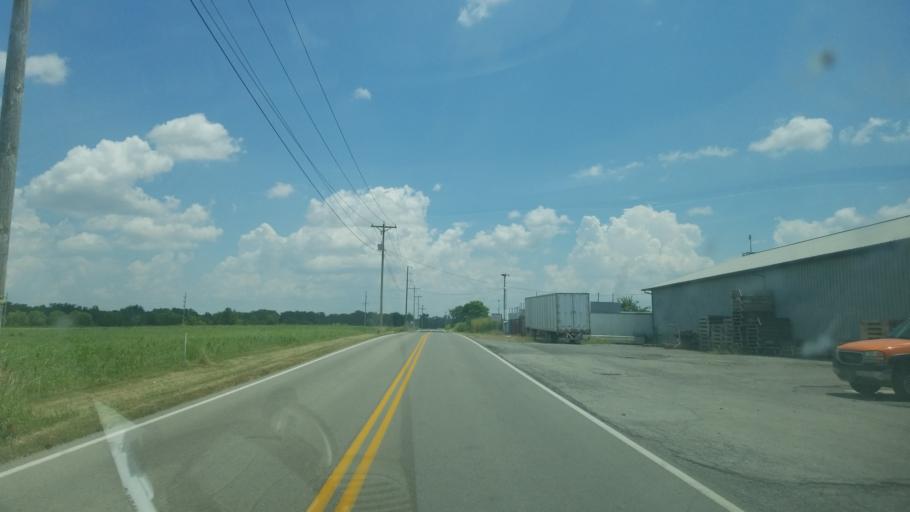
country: US
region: Ohio
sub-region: Hardin County
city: Kenton
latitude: 40.6331
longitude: -83.5873
